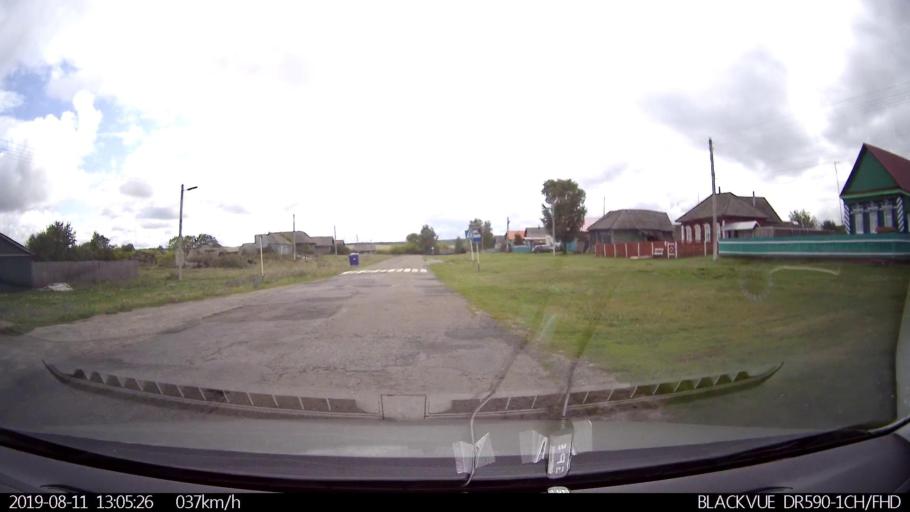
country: RU
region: Ulyanovsk
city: Ignatovka
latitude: 53.8706
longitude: 47.6496
